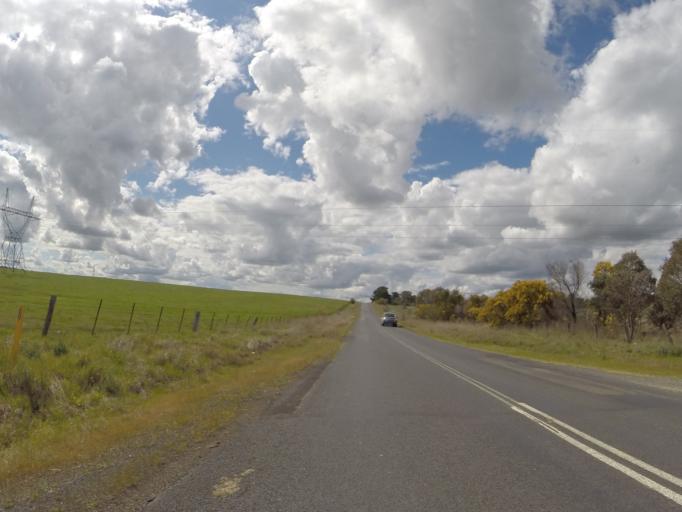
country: AU
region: New South Wales
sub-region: Yass Valley
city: Yass
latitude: -34.8717
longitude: 148.9127
